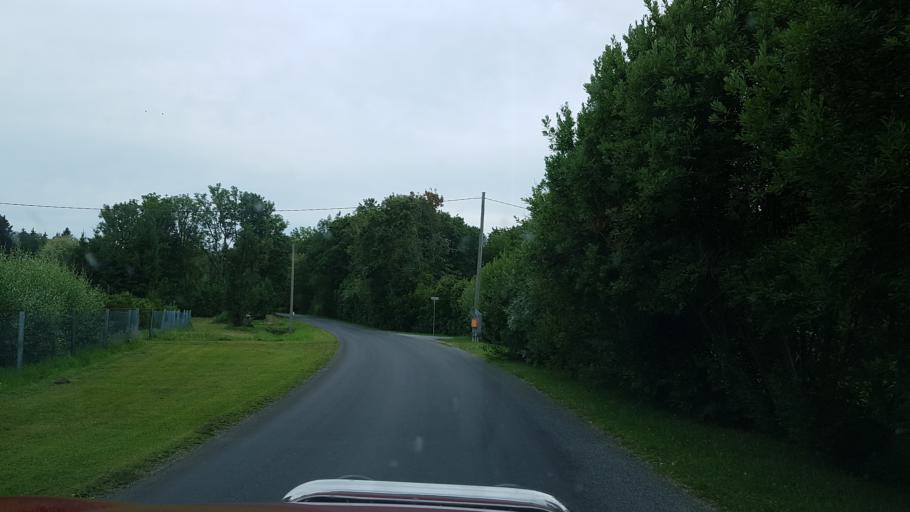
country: EE
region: Laeaene
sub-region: Ridala Parish
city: Uuemoisa
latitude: 59.0032
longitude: 23.7214
